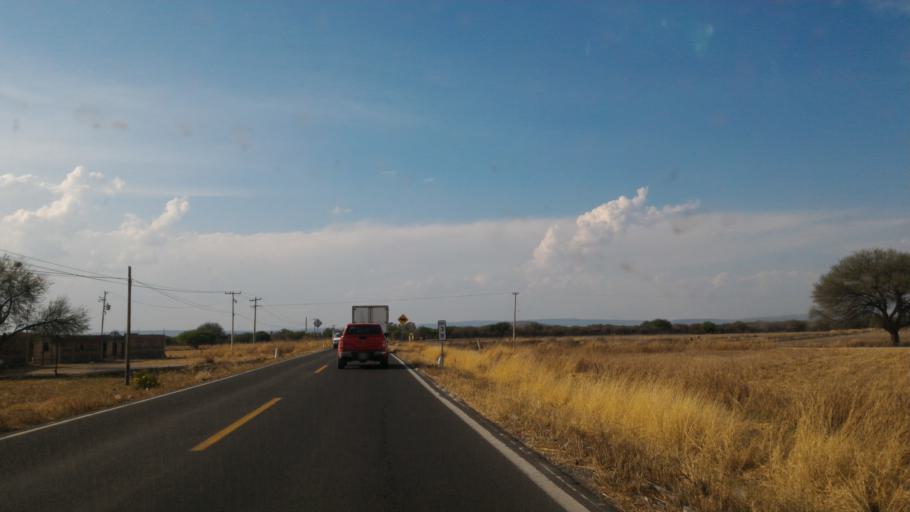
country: MX
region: Guanajuato
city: Ciudad Manuel Doblado
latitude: 20.7648
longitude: -101.9699
